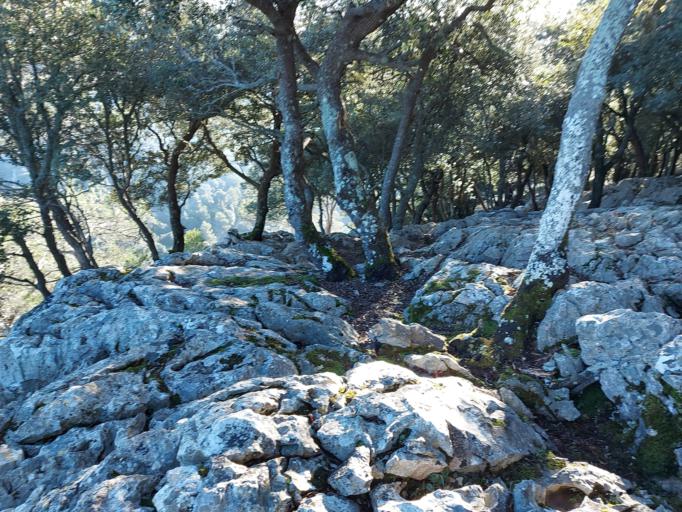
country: ES
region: Balearic Islands
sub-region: Illes Balears
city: Escorca
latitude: 39.8125
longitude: 2.8870
